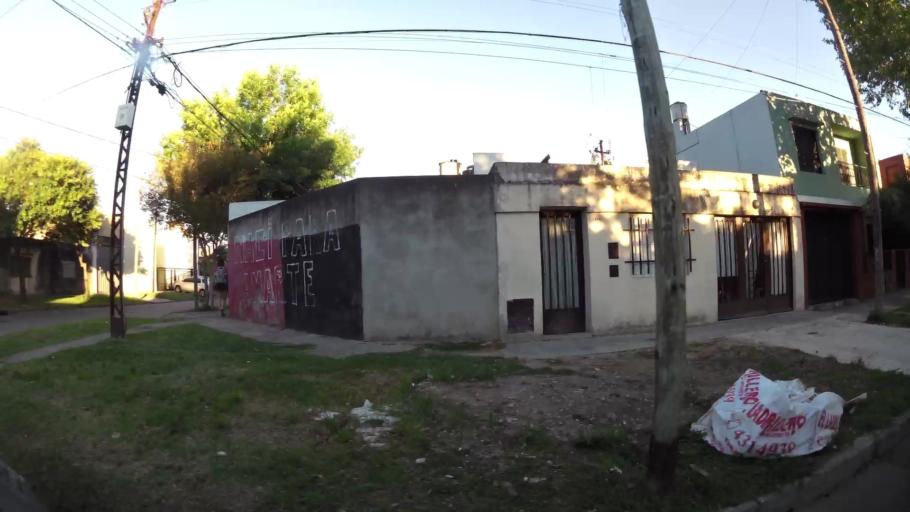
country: AR
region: Santa Fe
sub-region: Departamento de Rosario
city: Rosario
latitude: -32.9654
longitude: -60.6701
